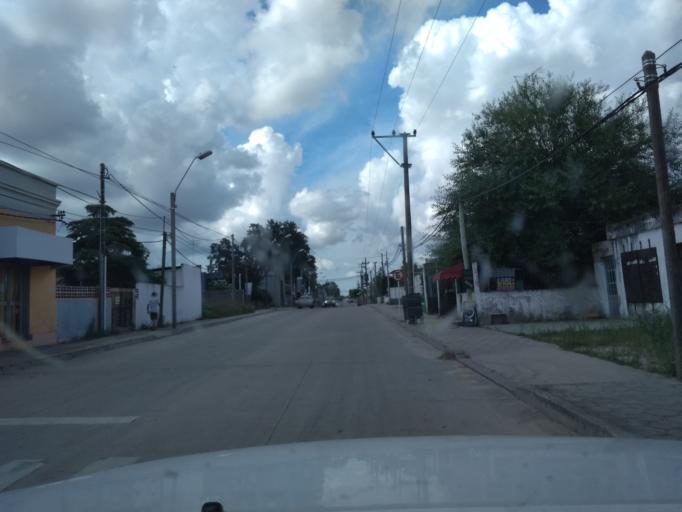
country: UY
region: Florida
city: Florida
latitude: -34.0900
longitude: -56.2150
